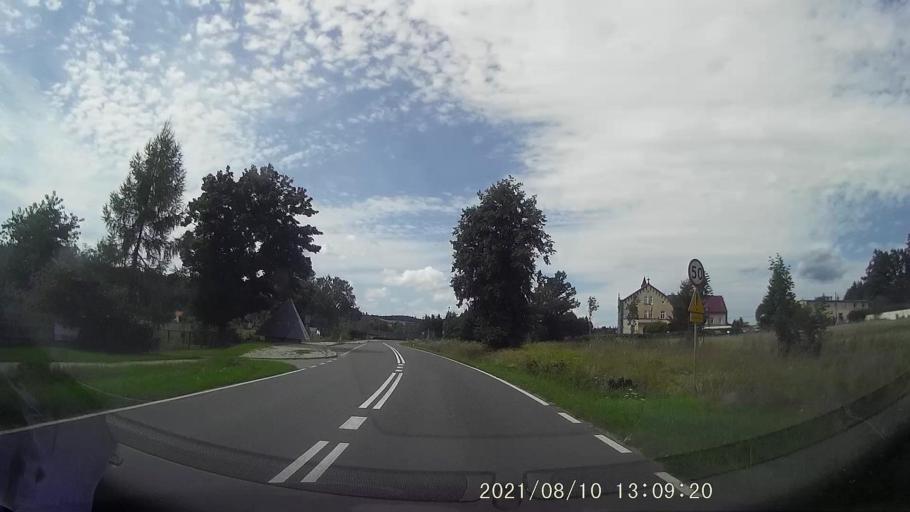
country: PL
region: Lower Silesian Voivodeship
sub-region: Powiat klodzki
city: Bozkow
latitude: 50.4975
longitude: 16.5414
